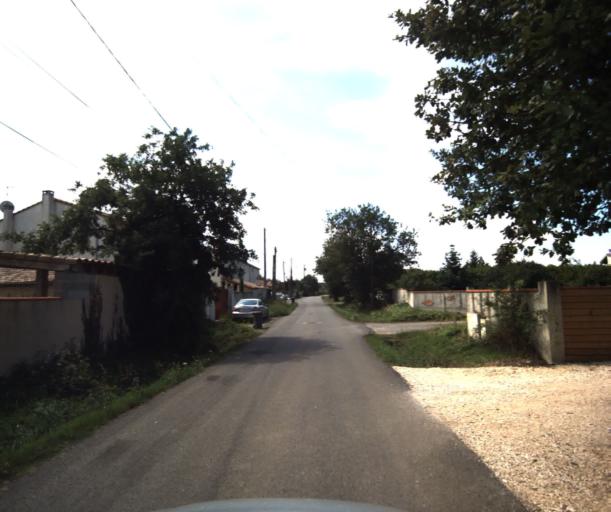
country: FR
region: Midi-Pyrenees
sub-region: Departement de la Haute-Garonne
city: Lacasse
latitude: 43.3918
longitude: 1.2640
